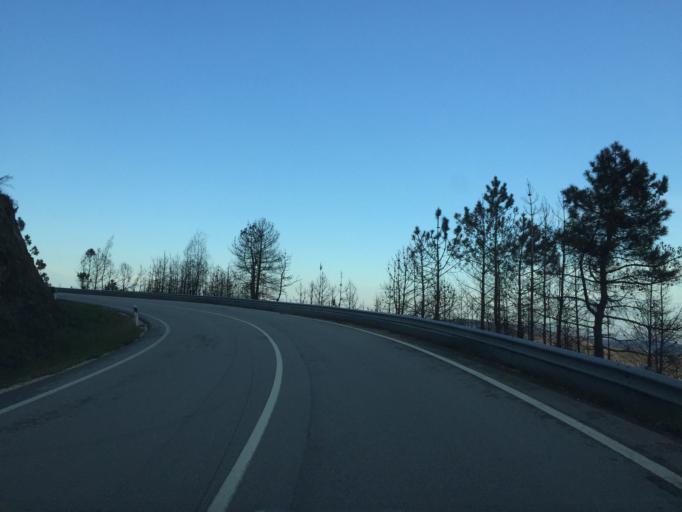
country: PT
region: Coimbra
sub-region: Gois
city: Gois
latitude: 40.1001
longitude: -8.0491
